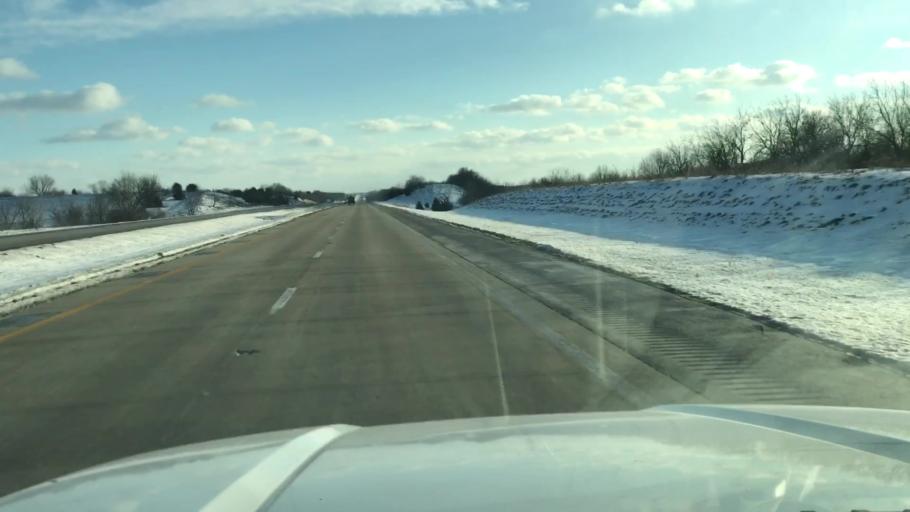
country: US
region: Missouri
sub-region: Andrew County
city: Savannah
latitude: 39.9529
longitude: -94.8604
